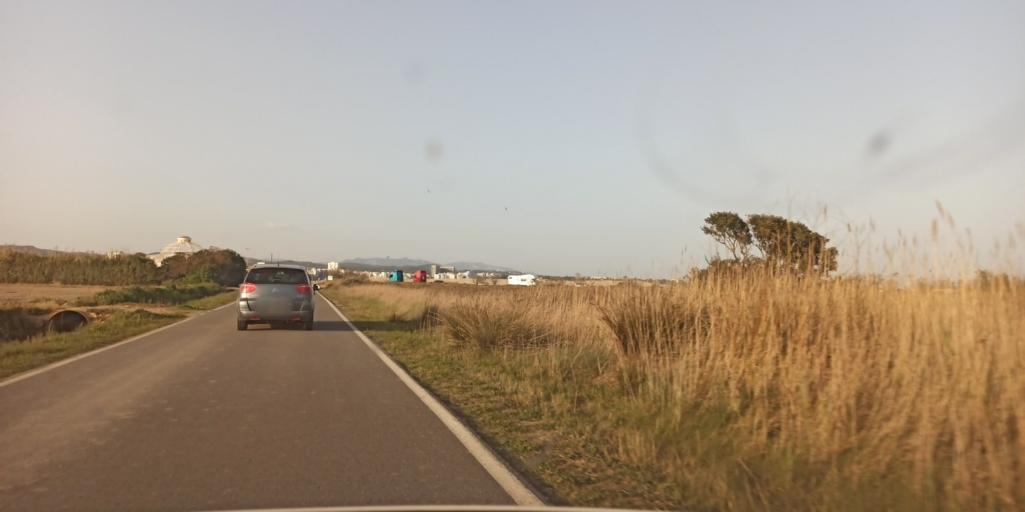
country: ES
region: Catalonia
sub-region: Provincia de Tarragona
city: L'Ampolla
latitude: 40.7957
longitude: 0.6997
